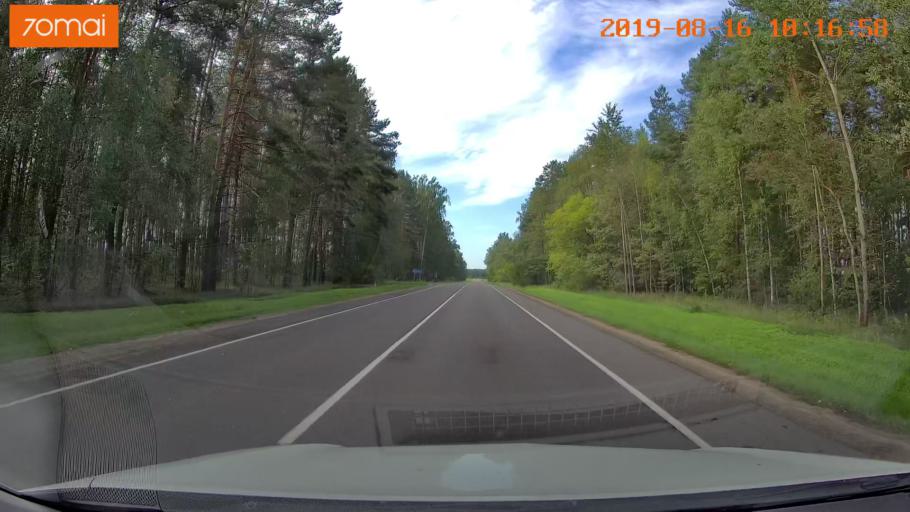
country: BY
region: Mogilev
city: Asipovichy
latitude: 53.3166
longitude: 28.7172
